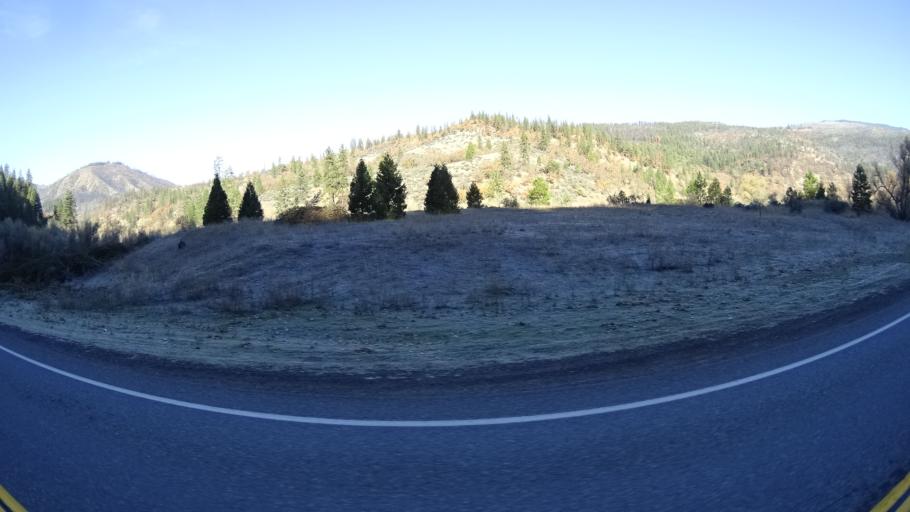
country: US
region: California
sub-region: Siskiyou County
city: Yreka
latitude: 41.8240
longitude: -122.9848
